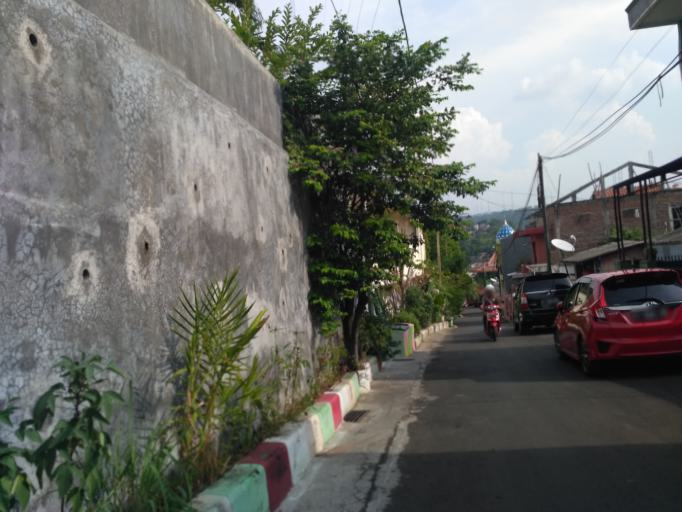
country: ID
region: Central Java
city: Semarang
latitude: -7.0131
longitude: 110.4459
